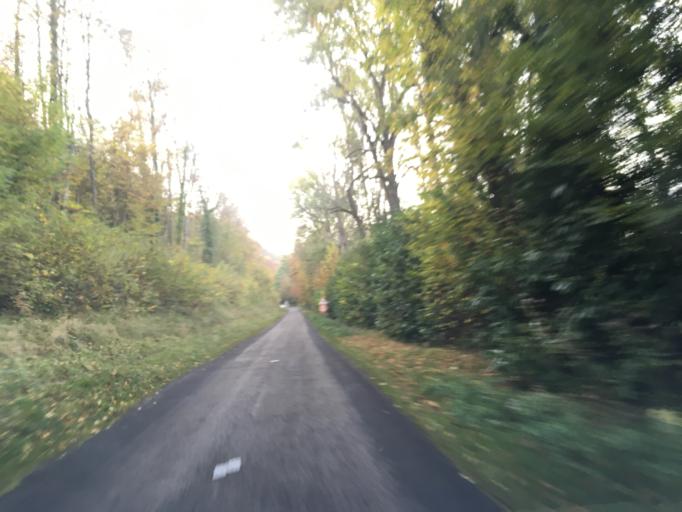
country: FR
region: Haute-Normandie
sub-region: Departement de l'Eure
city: Heudreville-sur-Eure
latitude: 49.1096
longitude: 1.2149
